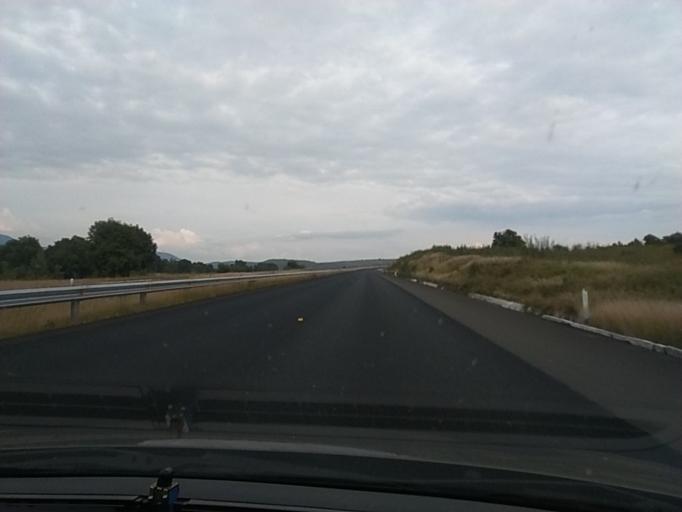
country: MX
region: Mexico
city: Huaniqueo de Morales
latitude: 19.8894
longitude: -101.5240
